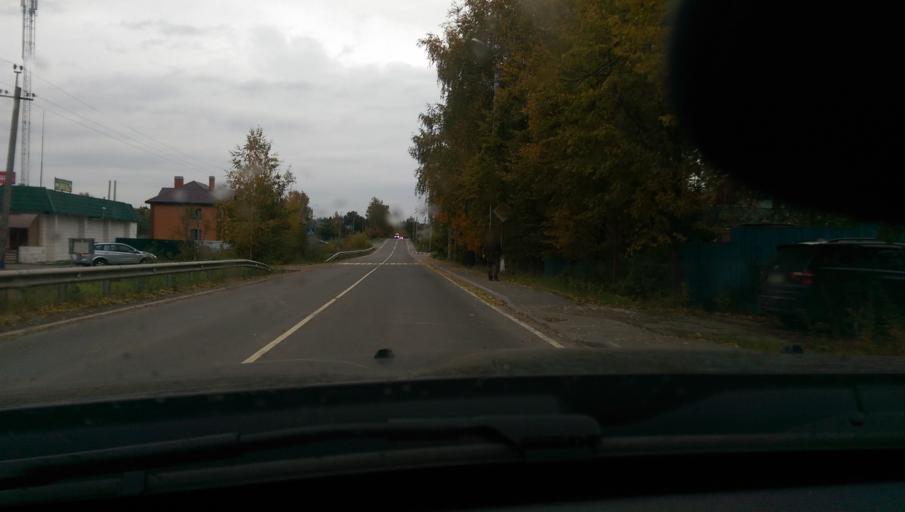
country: RU
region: Moskovskaya
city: Pirogovskiy
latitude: 56.0134
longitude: 37.7186
